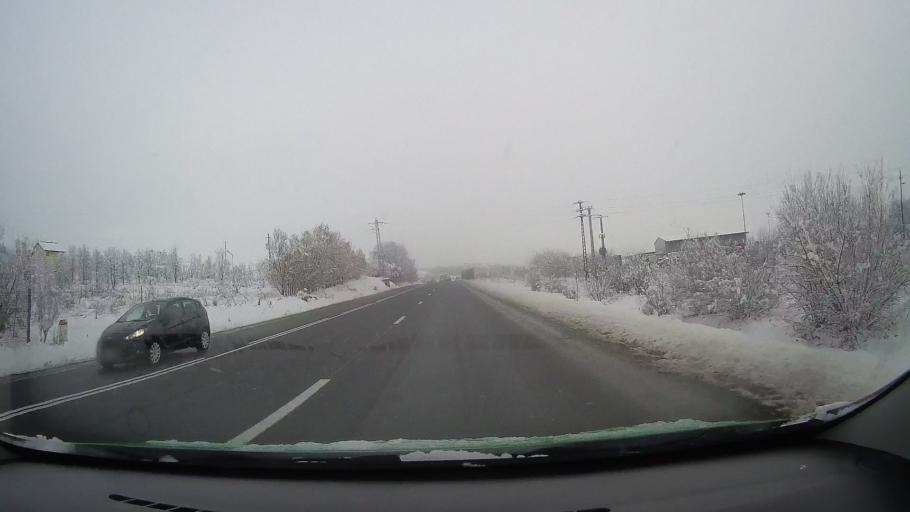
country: RO
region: Sibiu
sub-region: Comuna Cristian
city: Cristian
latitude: 45.7884
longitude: 24.0457
